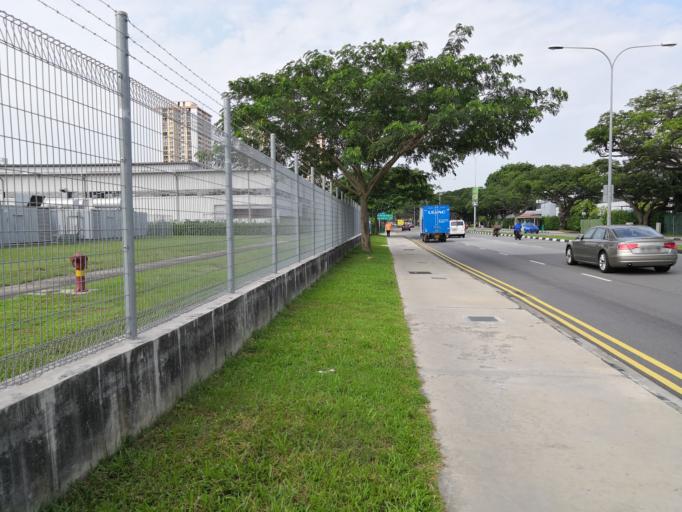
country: SG
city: Singapore
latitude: 1.3185
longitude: 103.9305
